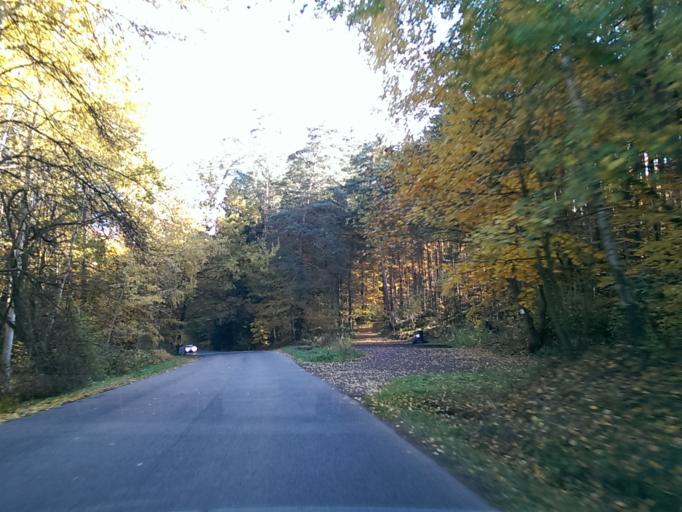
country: CZ
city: Prisovice
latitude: 50.5623
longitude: 15.1131
